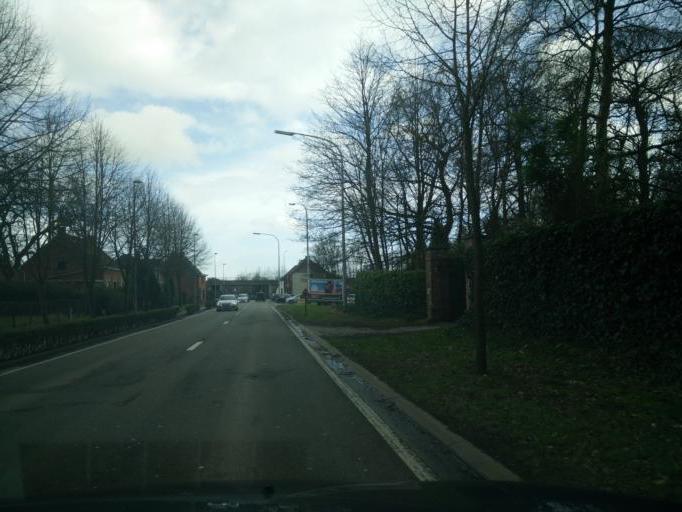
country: BE
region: Flanders
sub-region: Provincie Oost-Vlaanderen
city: Laarne
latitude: 51.0339
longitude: 3.8224
